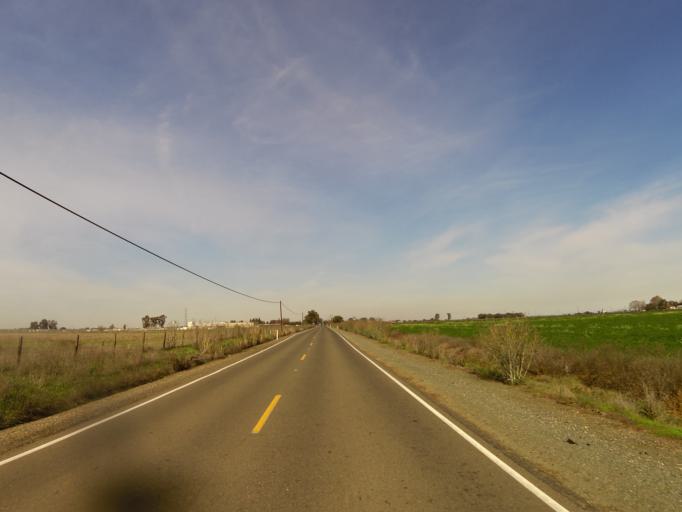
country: US
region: California
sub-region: San Joaquin County
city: Thornton
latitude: 38.2983
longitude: -121.4199
